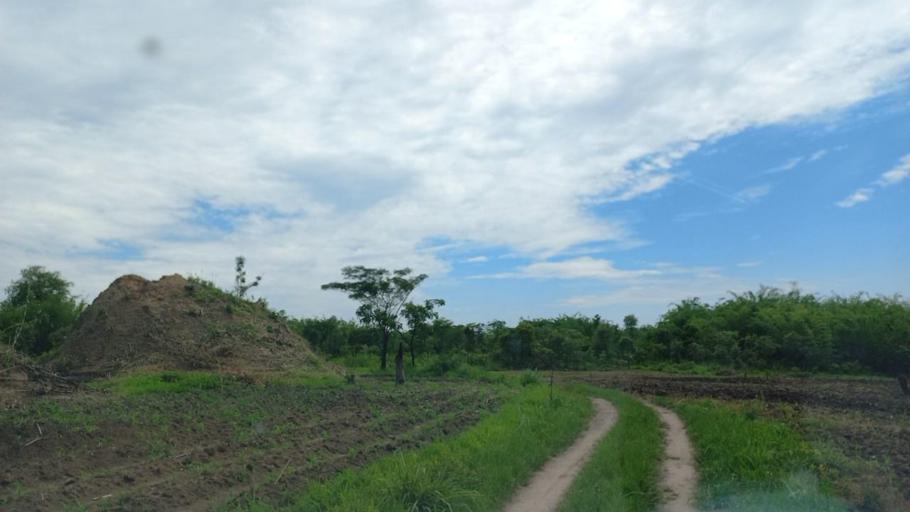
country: ZM
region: Copperbelt
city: Kitwe
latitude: -12.7897
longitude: 28.3918
